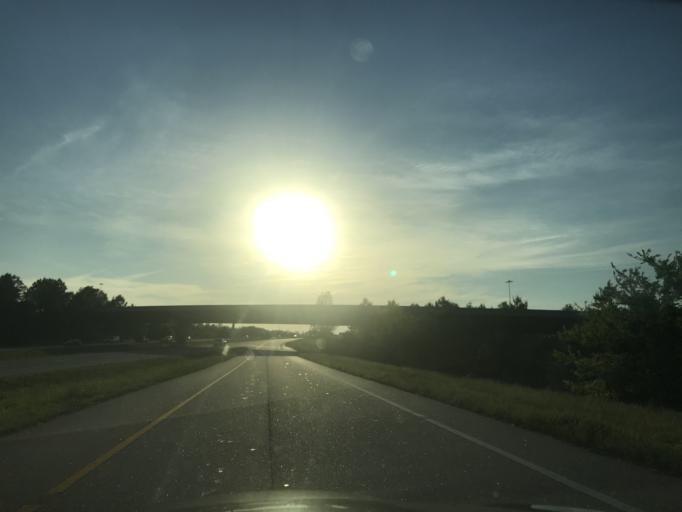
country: US
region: North Carolina
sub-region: Wake County
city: Raleigh
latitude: 35.8750
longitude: -78.5728
